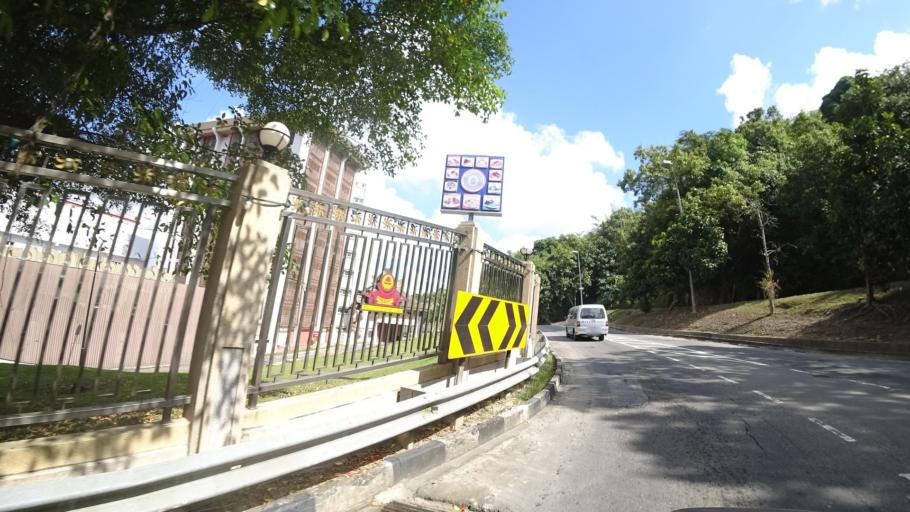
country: BN
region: Brunei and Muara
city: Bandar Seri Begawan
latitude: 4.8850
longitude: 114.9505
